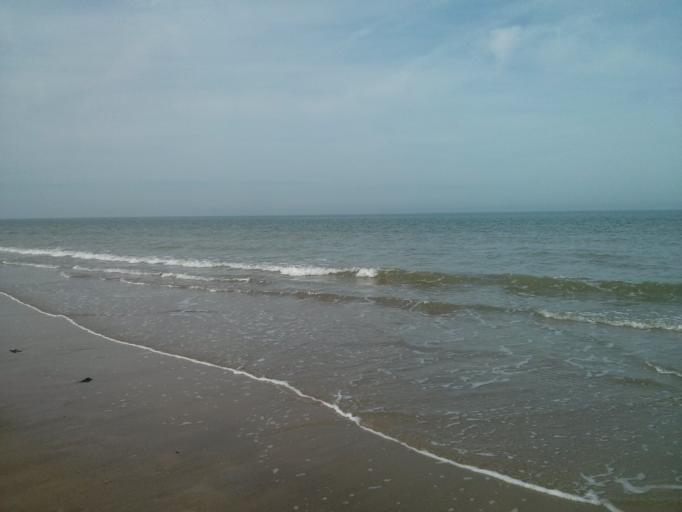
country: NL
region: Zeeland
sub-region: Gemeente Veere
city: Veere
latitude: 51.5956
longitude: 3.5772
